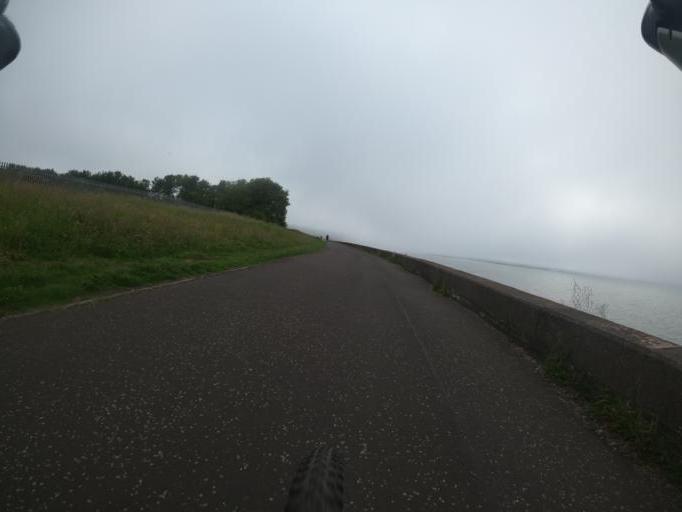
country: GB
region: Scotland
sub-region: Edinburgh
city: Edinburgh
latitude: 55.9837
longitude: -3.2504
